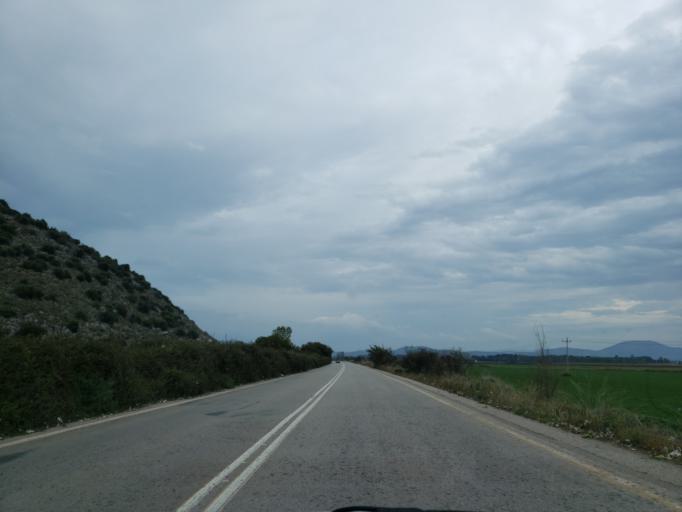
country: GR
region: Central Greece
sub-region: Nomos Voiotias
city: Akraifnia
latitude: 38.4772
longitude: 23.1100
